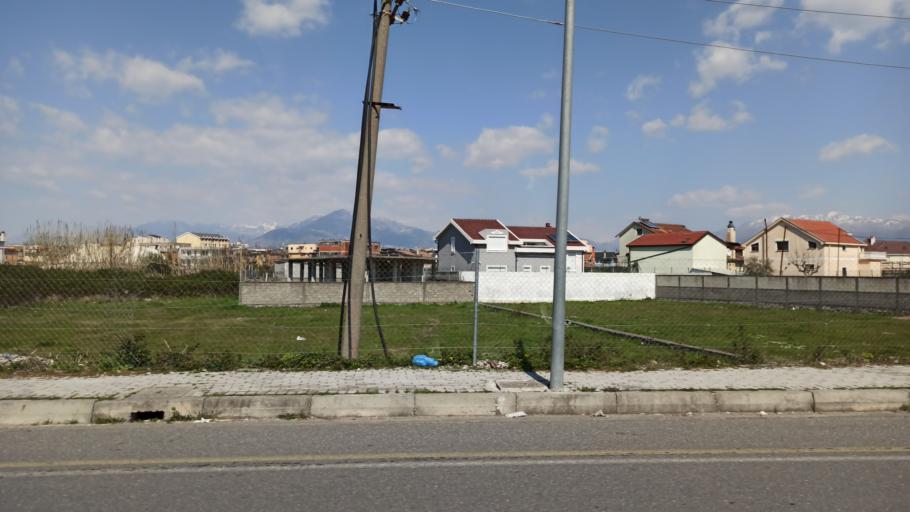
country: AL
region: Shkoder
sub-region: Rrethi i Shkodres
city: Shkoder
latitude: 42.0563
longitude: 19.5095
